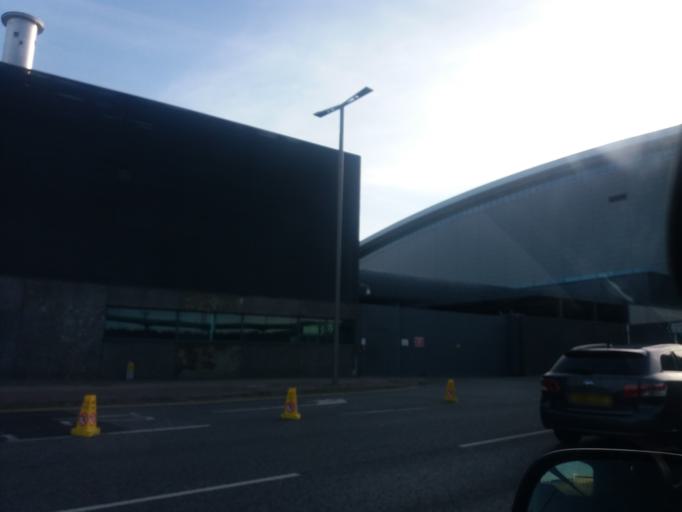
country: IE
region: Leinster
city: Beaumont
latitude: 53.4255
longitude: -6.2379
